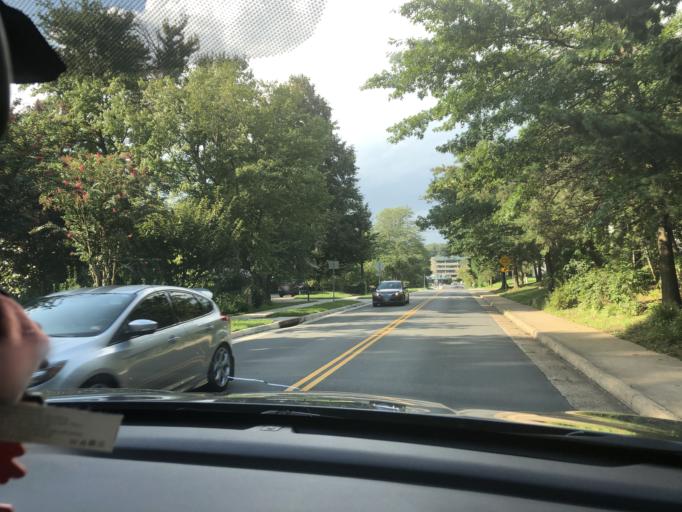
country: US
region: Virginia
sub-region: City of Fairfax
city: Fairfax
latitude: 38.8404
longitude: -77.2881
